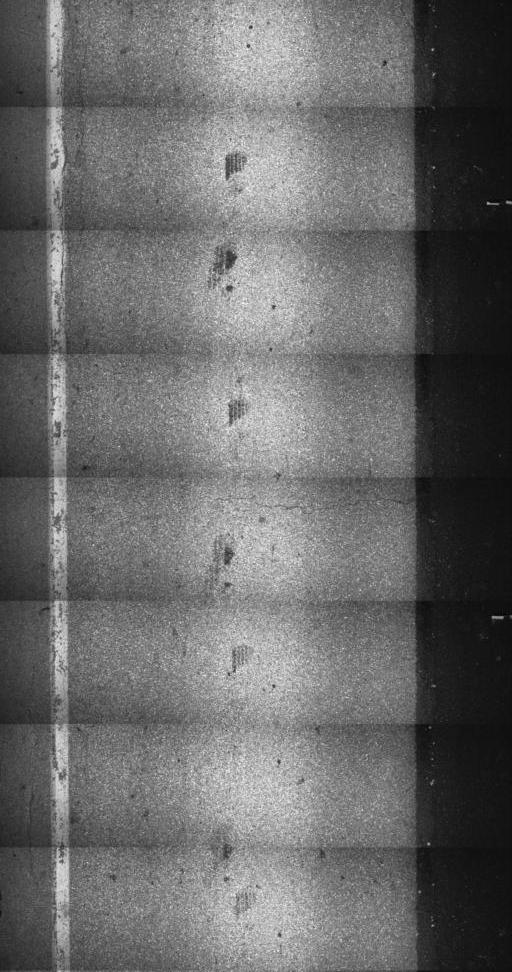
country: US
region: Vermont
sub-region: Chittenden County
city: Milton
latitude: 44.6752
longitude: -73.1110
